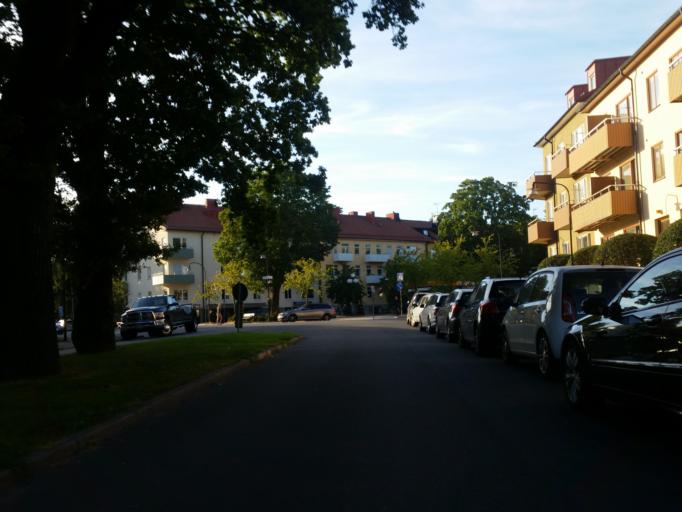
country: SE
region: Stockholm
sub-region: Solna Kommun
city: Solna
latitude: 59.3197
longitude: 17.9888
